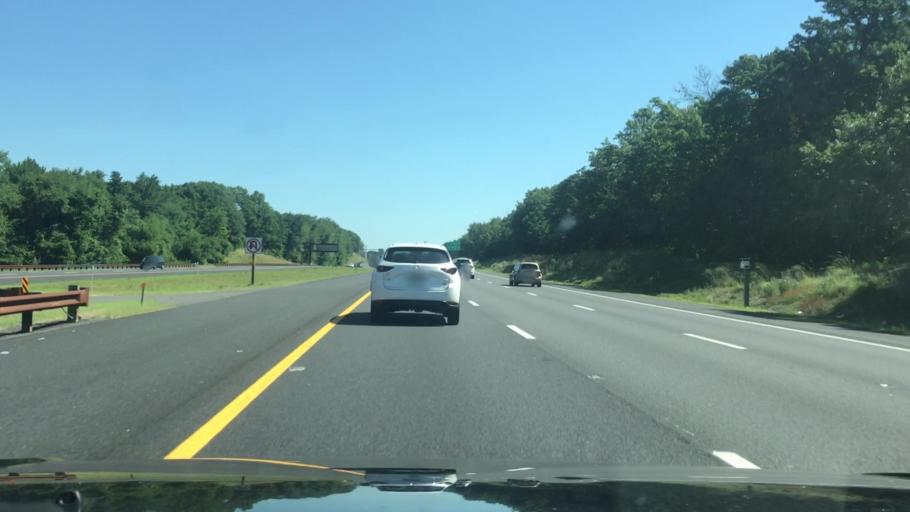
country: US
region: New Jersey
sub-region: Monmouth County
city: Ramtown
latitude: 40.0865
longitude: -74.1504
